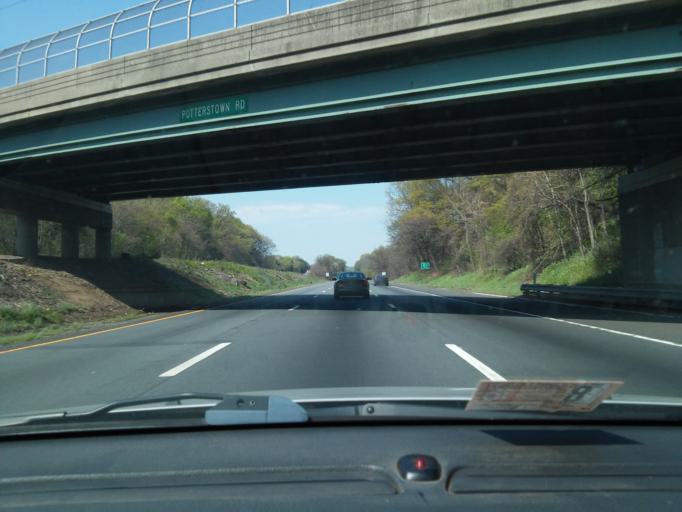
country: US
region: New Jersey
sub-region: Hunterdon County
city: Whitehouse Station
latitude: 40.6508
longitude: -74.7908
